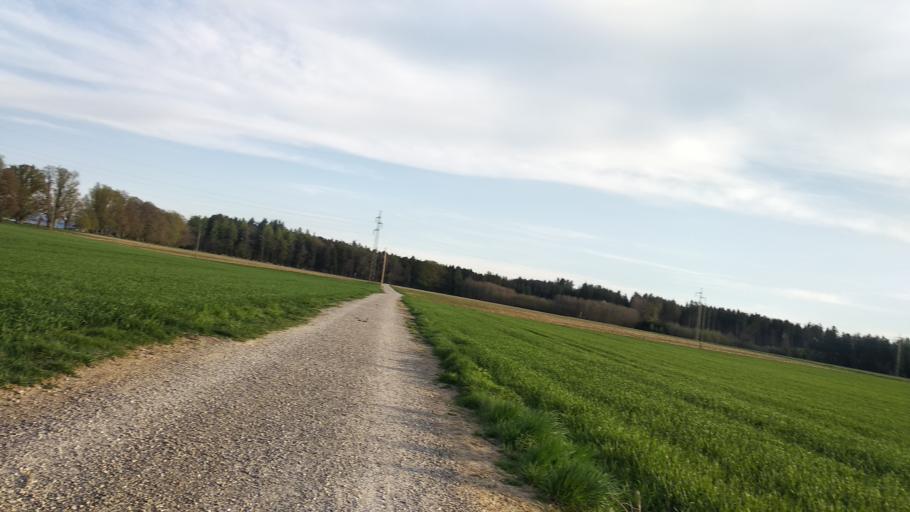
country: DE
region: Bavaria
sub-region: Swabia
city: Memmingen
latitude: 47.9646
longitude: 10.1786
